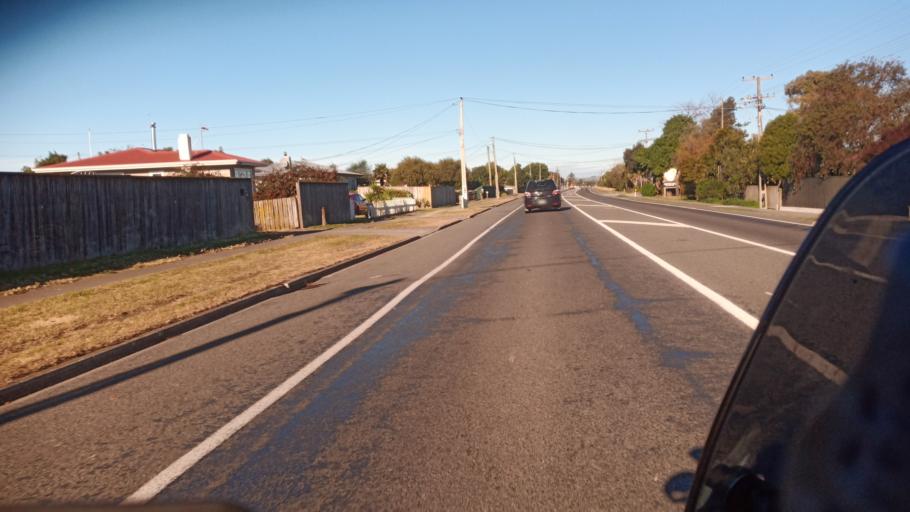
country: NZ
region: Hawke's Bay
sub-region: Napier City
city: Napier
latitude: -39.4309
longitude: 176.8717
